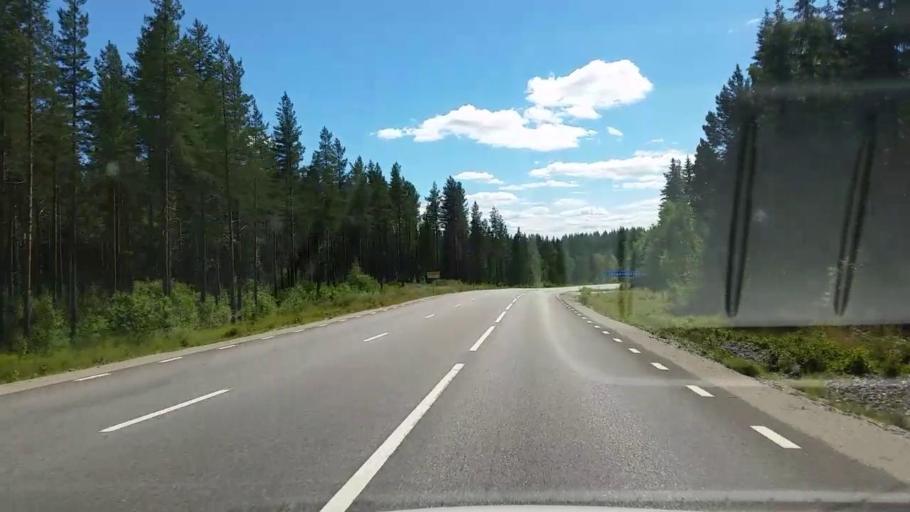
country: SE
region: Gaevleborg
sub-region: Bollnas Kommun
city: Vittsjo
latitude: 61.0516
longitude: 15.8011
